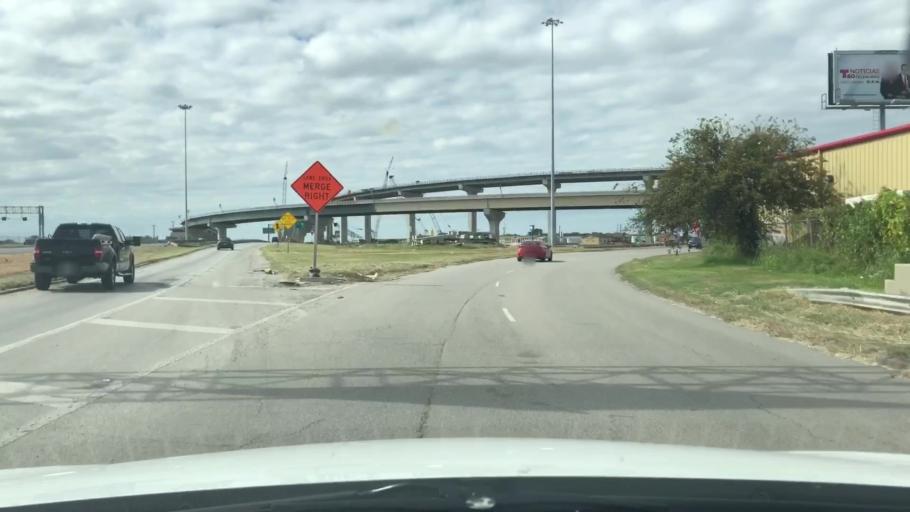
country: US
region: Texas
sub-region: Bexar County
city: Lackland Air Force Base
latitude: 29.3983
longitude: -98.6471
